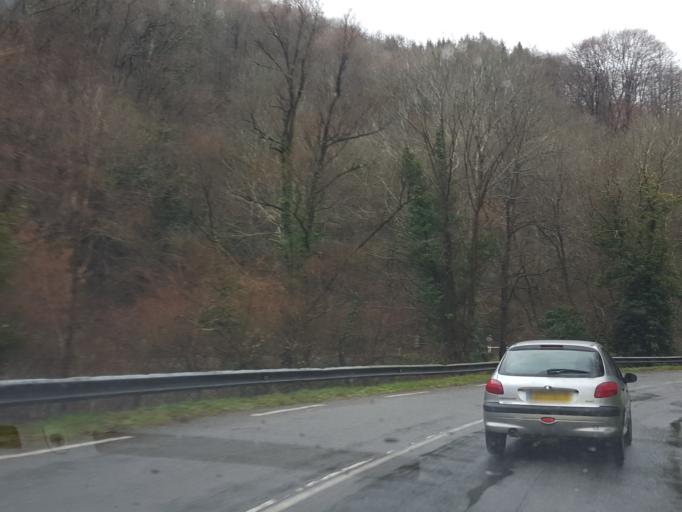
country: FR
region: Midi-Pyrenees
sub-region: Departement de l'Ariege
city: Saint-Girons
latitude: 42.9178
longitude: 1.1919
